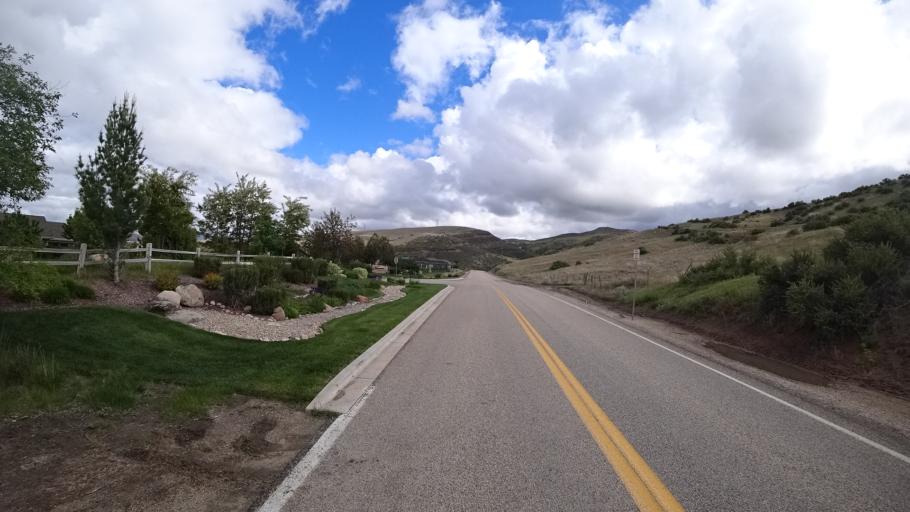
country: US
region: Idaho
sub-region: Ada County
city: Garden City
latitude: 43.7238
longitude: -116.2349
